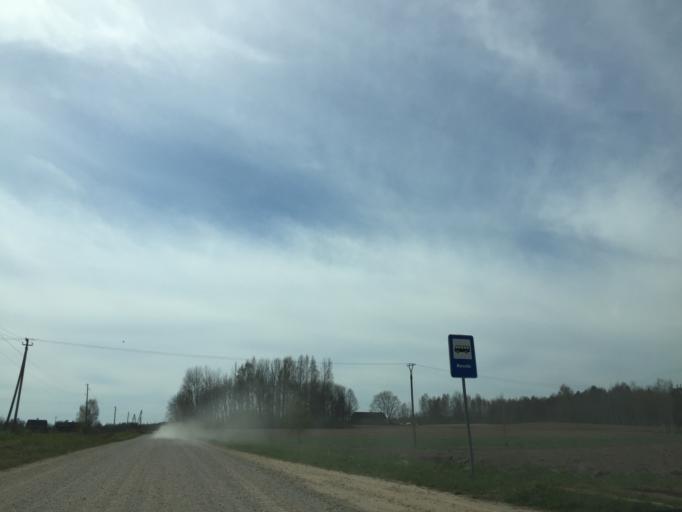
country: LV
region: Ludzas Rajons
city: Ludza
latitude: 56.5581
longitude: 27.5397
